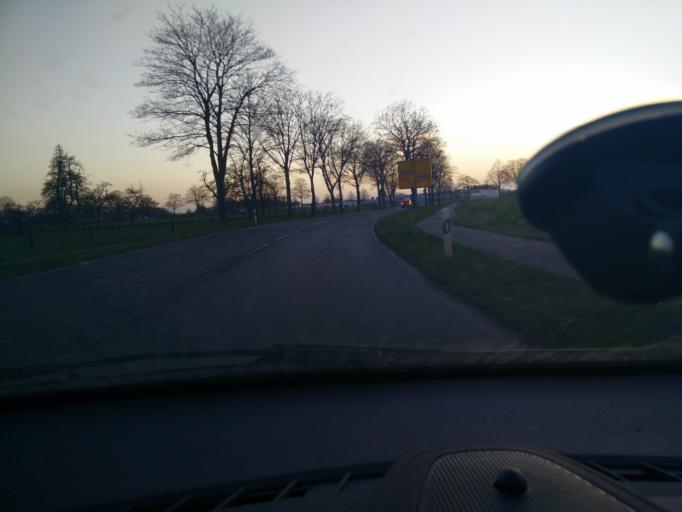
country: DE
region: North Rhine-Westphalia
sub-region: Regierungsbezirk Dusseldorf
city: Wesel
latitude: 51.7330
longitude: 6.6976
